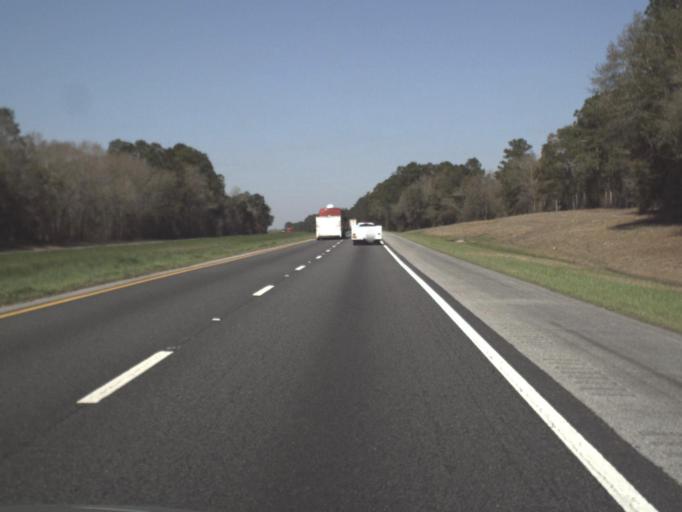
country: US
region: Florida
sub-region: Jackson County
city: Sneads
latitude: 30.6668
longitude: -85.0555
